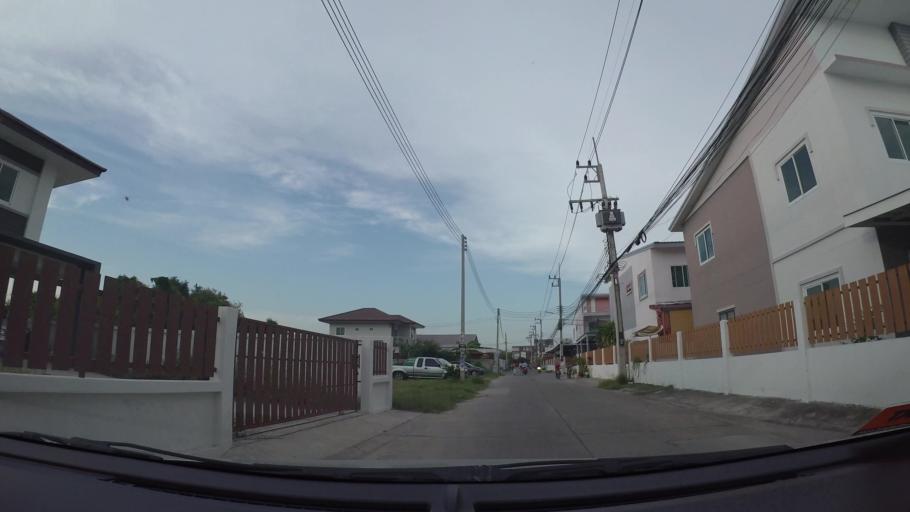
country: TH
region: Chon Buri
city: Chon Buri
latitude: 13.3368
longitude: 100.9824
